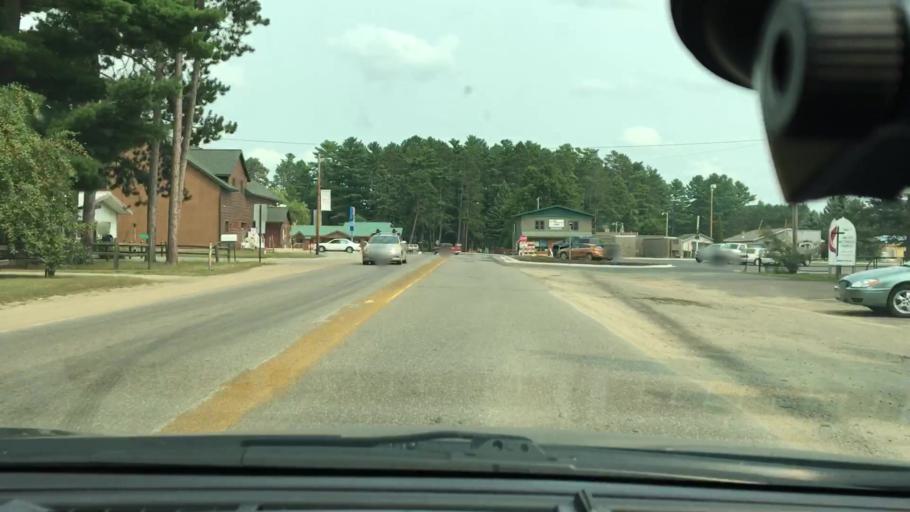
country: US
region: Minnesota
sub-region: Crow Wing County
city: Cross Lake
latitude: 46.7309
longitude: -93.9597
